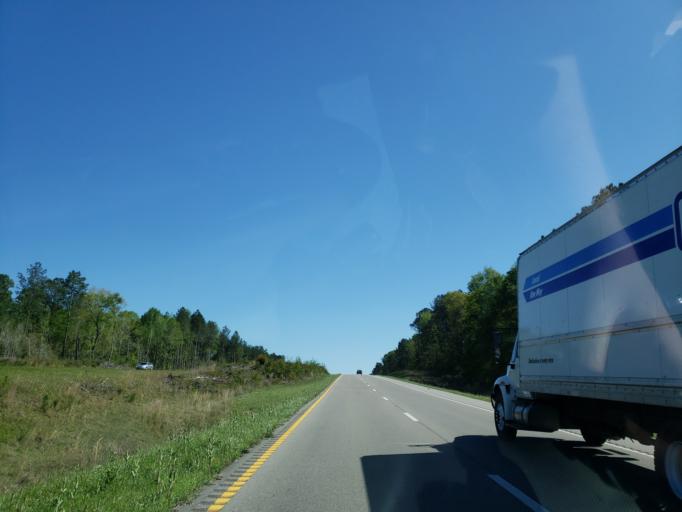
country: US
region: Mississippi
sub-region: Stone County
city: Wiggins
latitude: 30.9688
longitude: -89.1955
